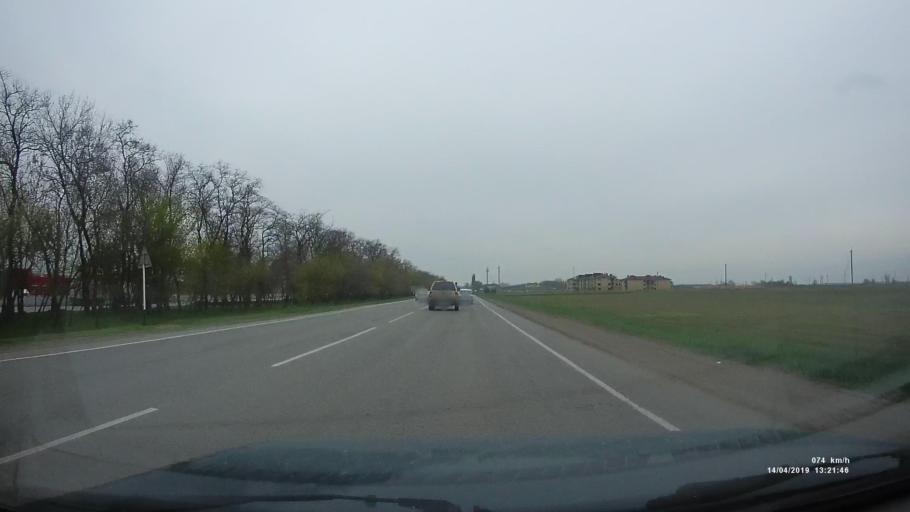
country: RU
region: Rostov
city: Kuleshovka
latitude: 47.0819
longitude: 39.5197
